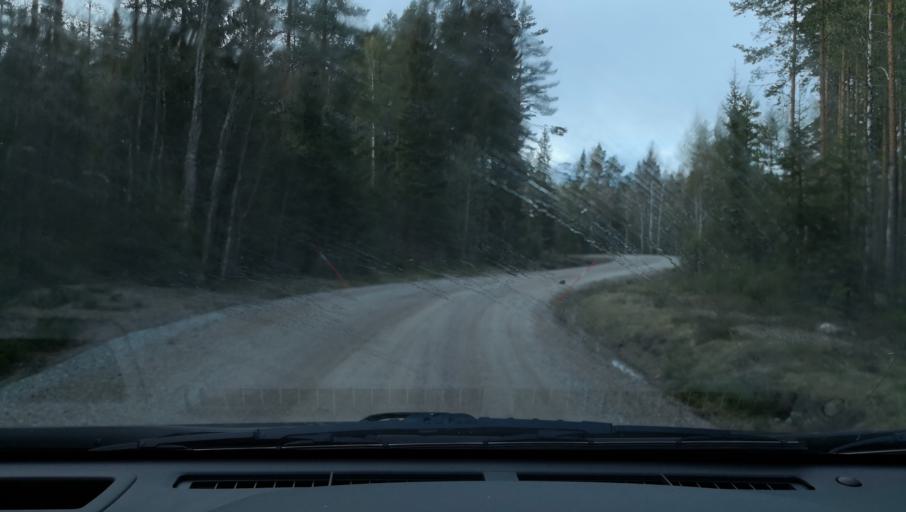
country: SE
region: Dalarna
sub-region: Saters Kommun
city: Saeter
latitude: 60.1764
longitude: 15.7254
